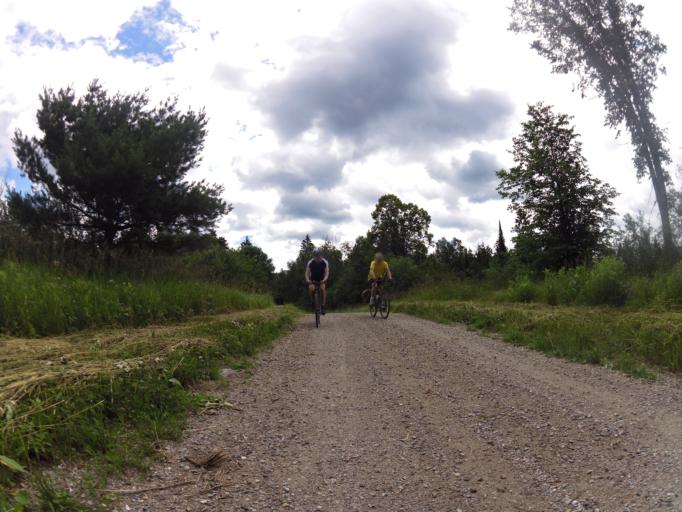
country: CA
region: Ontario
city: Perth
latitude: 45.0267
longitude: -76.5455
